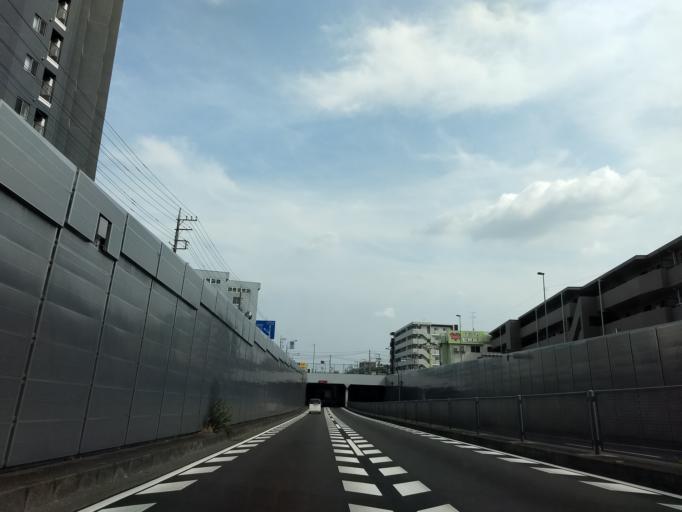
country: JP
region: Tokyo
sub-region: Machida-shi
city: Machida
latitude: 35.5174
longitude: 139.4548
